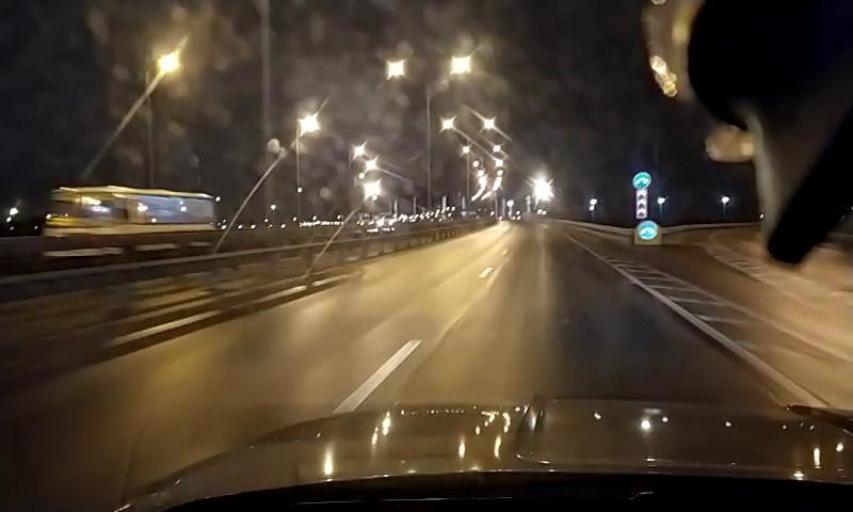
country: RU
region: Leningrad
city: Bugry
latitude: 60.0947
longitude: 30.3747
